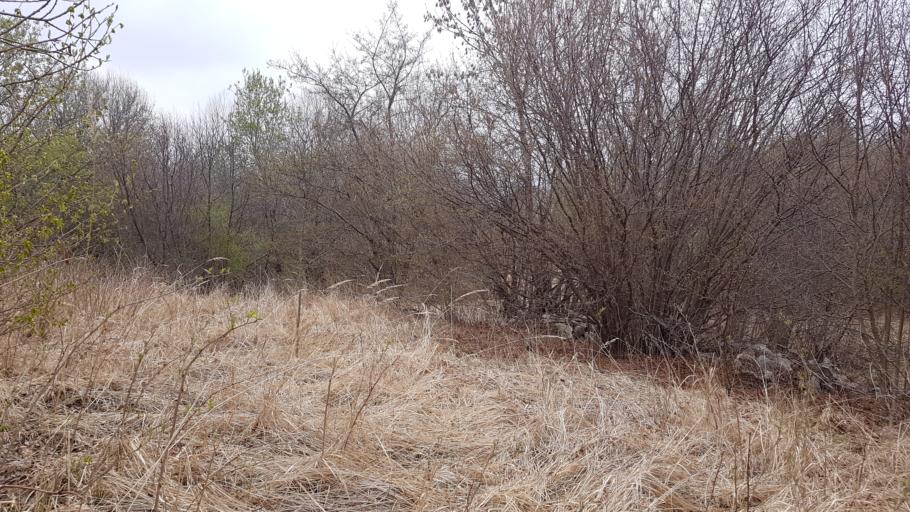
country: IT
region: Friuli Venezia Giulia
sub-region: Provincia di Udine
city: Faedis
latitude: 46.1878
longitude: 13.3799
